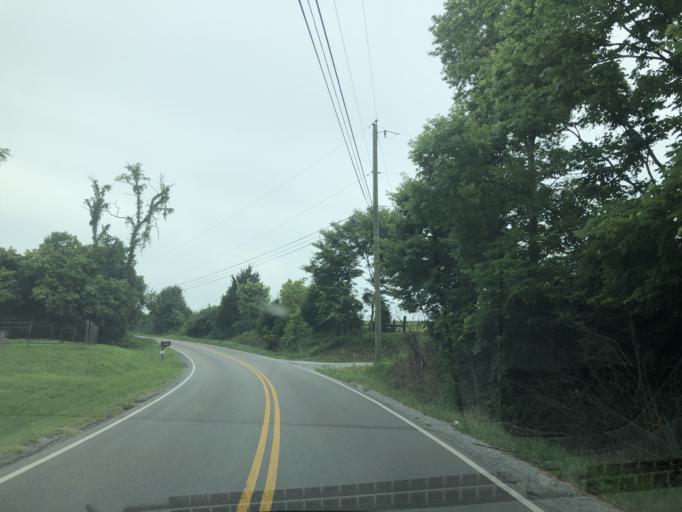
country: US
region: Tennessee
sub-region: Williamson County
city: Nolensville
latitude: 36.0344
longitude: -86.6865
